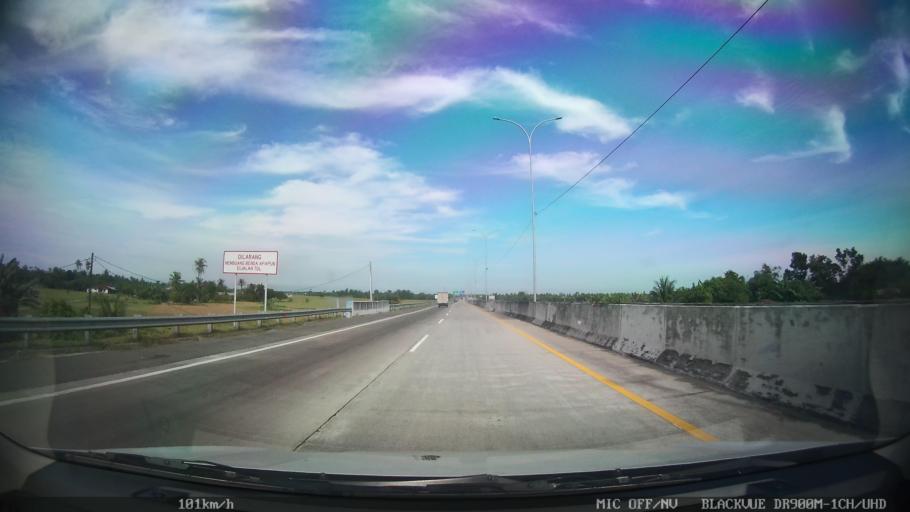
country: ID
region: North Sumatra
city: Sunggal
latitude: 3.6415
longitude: 98.5685
